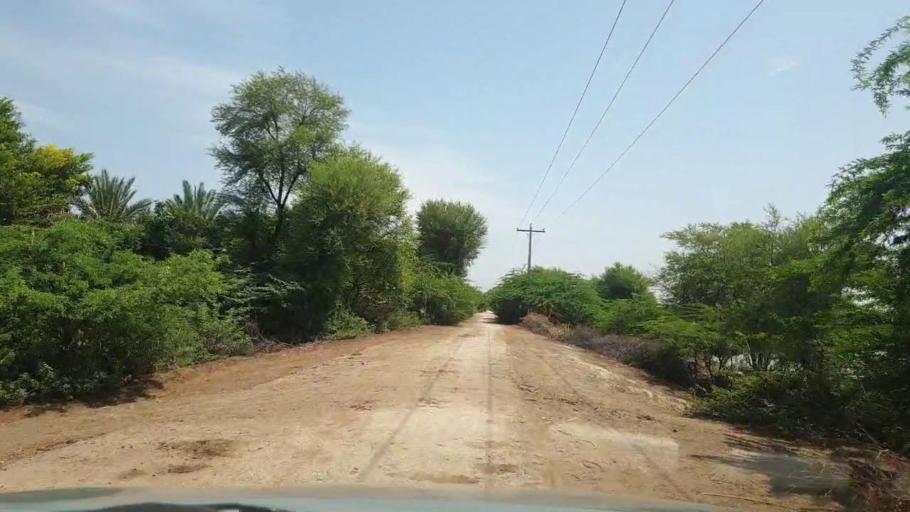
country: PK
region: Sindh
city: Bozdar
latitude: 27.1081
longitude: 68.9826
